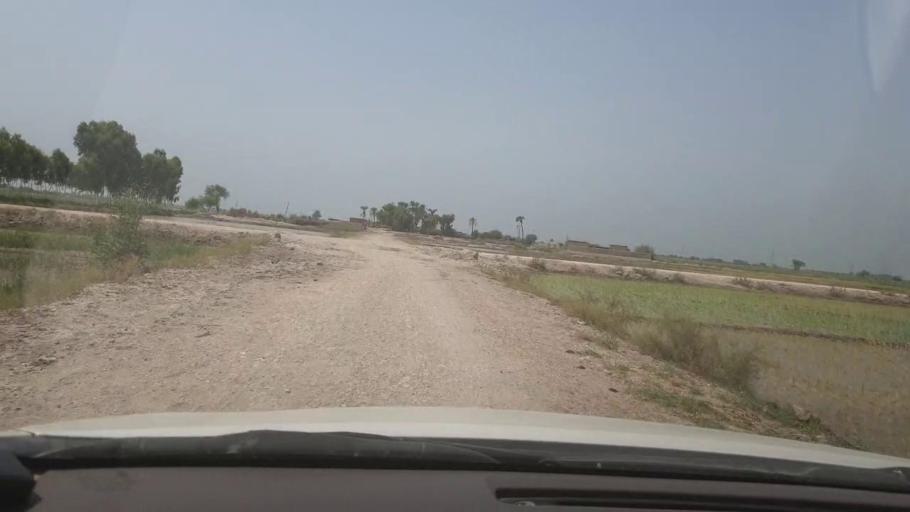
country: PK
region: Sindh
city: Shikarpur
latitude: 27.9602
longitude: 68.5919
